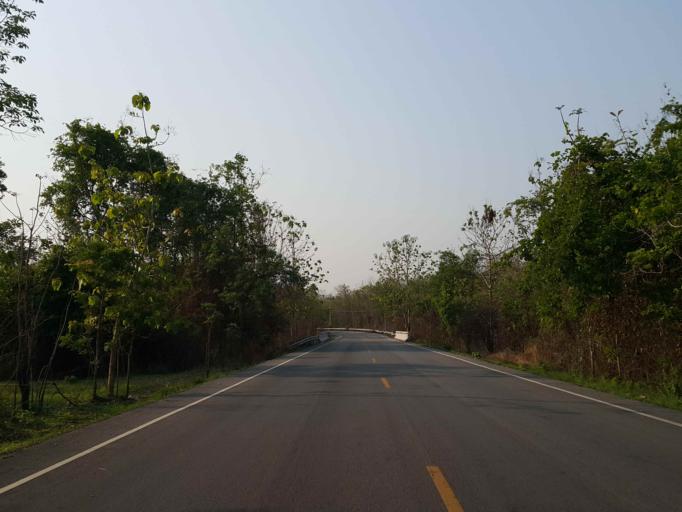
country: TH
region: Sukhothai
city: Thung Saliam
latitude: 17.3627
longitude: 99.4121
